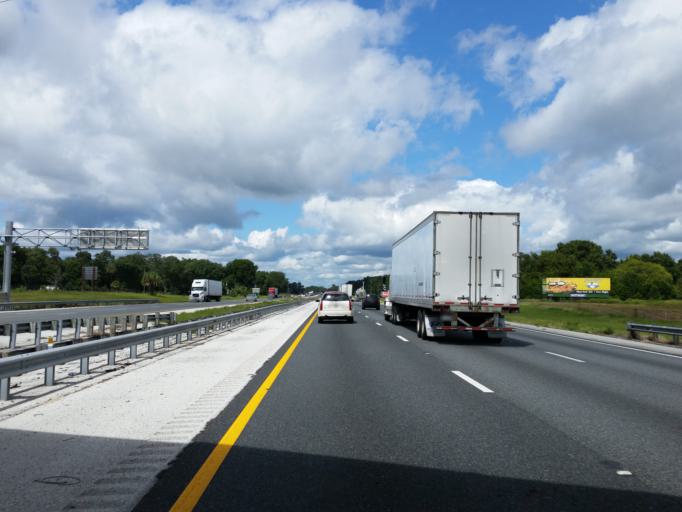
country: US
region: Florida
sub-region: Sumter County
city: Wildwood
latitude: 28.8946
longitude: -82.1004
